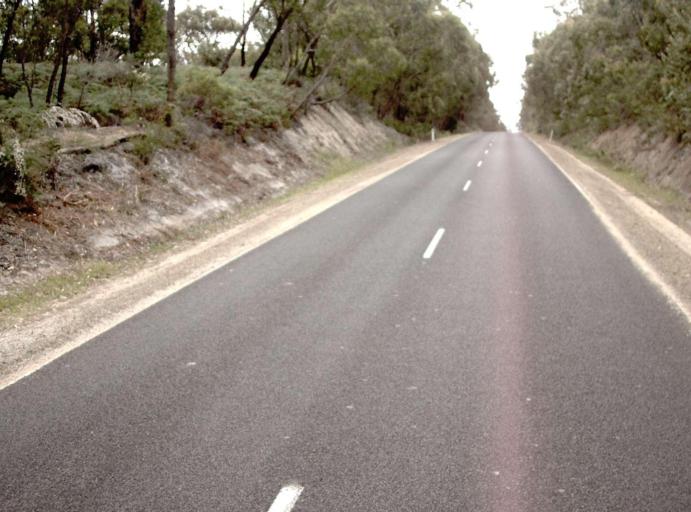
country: AU
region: Victoria
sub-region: Latrobe
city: Traralgon
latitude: -38.3981
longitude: 146.8171
